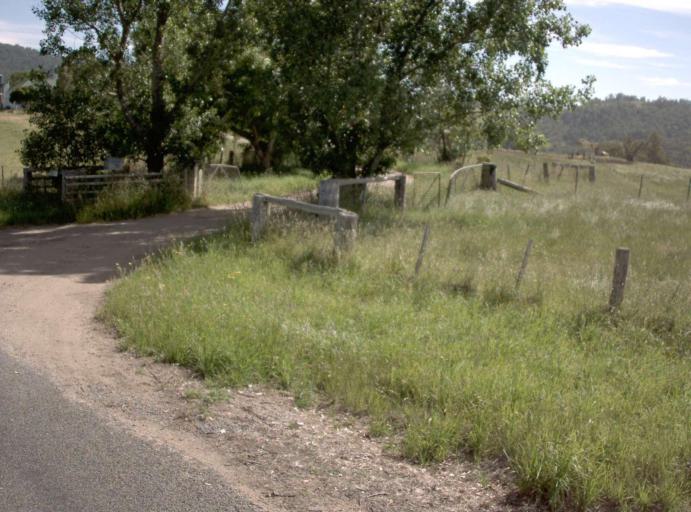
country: AU
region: Victoria
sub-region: East Gippsland
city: Lakes Entrance
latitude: -37.4909
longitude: 148.1306
